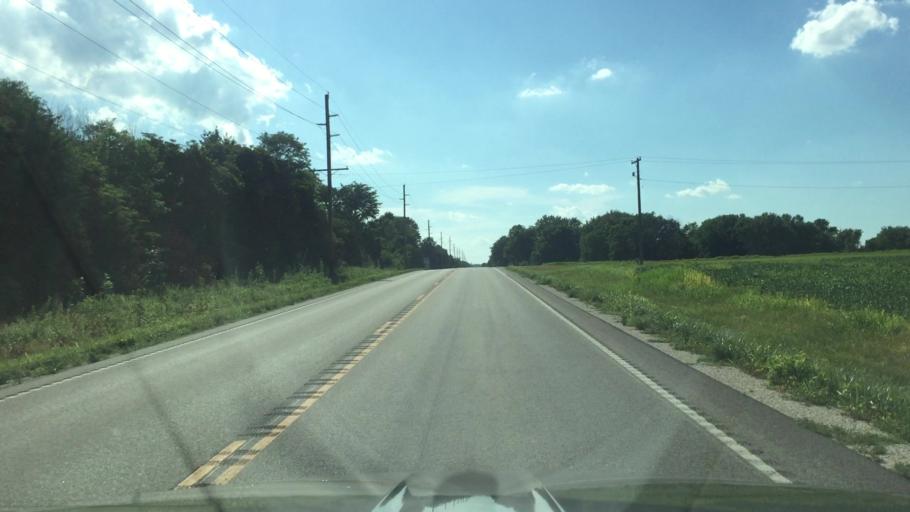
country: US
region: Missouri
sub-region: Morgan County
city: Versailles
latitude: 38.3971
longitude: -92.7275
